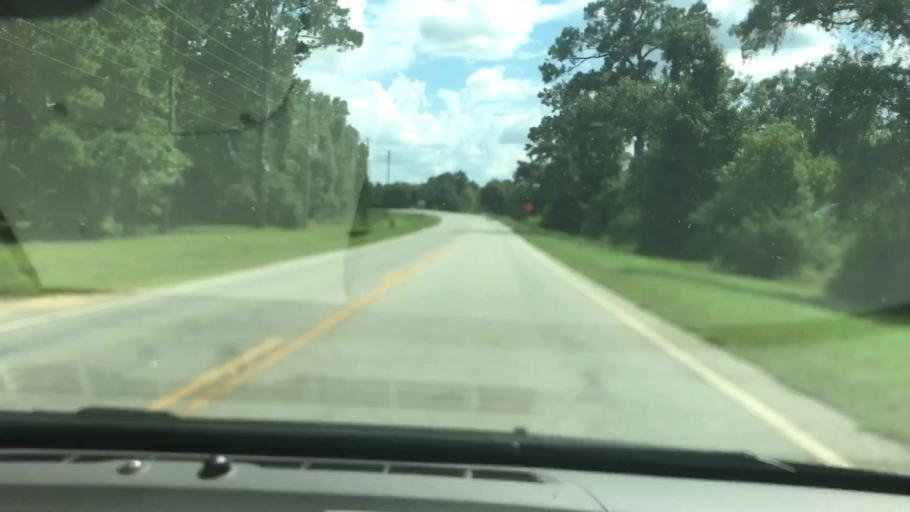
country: US
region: Georgia
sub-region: Clay County
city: Fort Gaines
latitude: 31.6552
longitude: -85.0474
